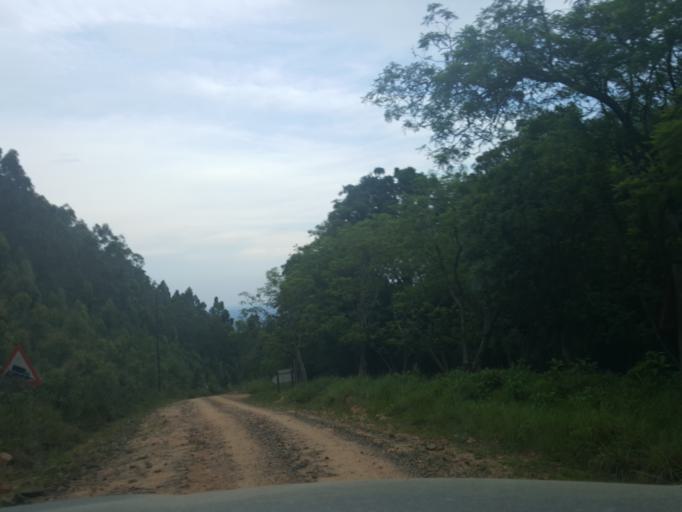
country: ZA
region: Limpopo
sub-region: Mopani District Municipality
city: Hoedspruit
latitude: -24.5960
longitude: 30.8690
